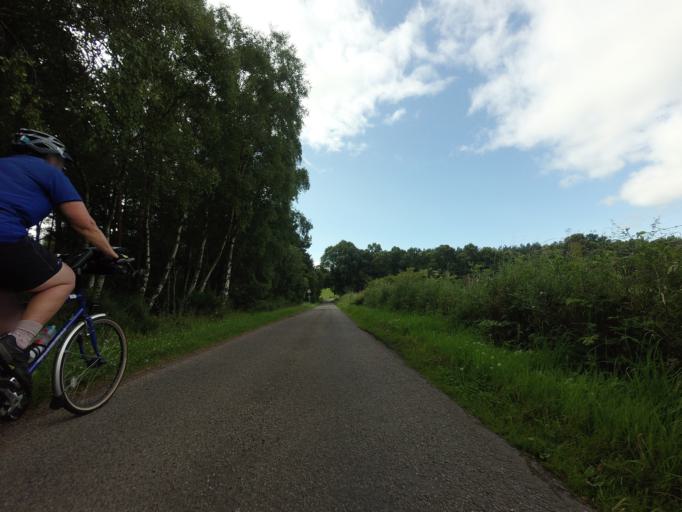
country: GB
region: Scotland
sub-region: Highland
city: Nairn
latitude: 57.5617
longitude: -3.8672
